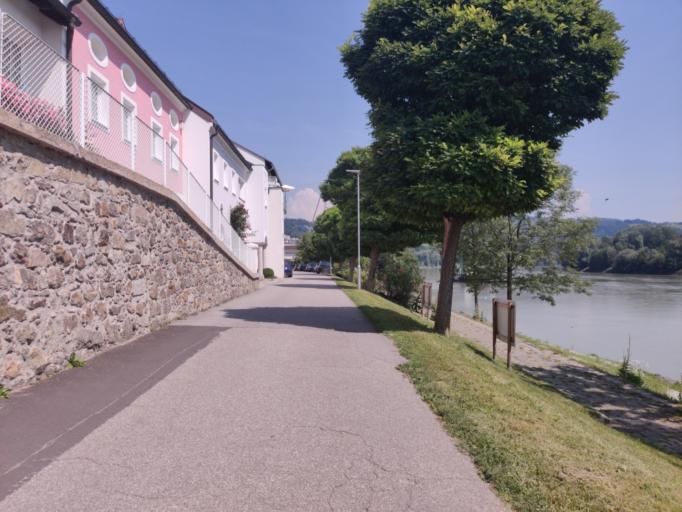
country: AT
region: Upper Austria
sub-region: Politischer Bezirk Urfahr-Umgebung
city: Ottensheim
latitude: 48.3295
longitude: 14.1745
